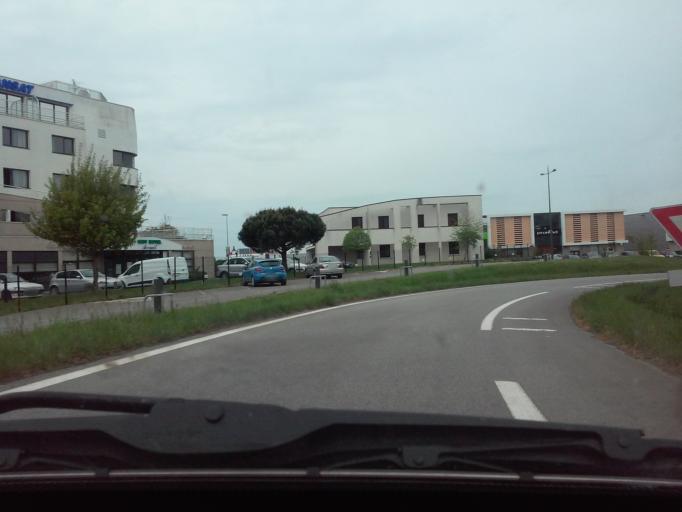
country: FR
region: Brittany
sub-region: Departement d'Ille-et-Vilaine
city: Saint-Jouan-des-Guerets
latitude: 48.6215
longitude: -1.9911
